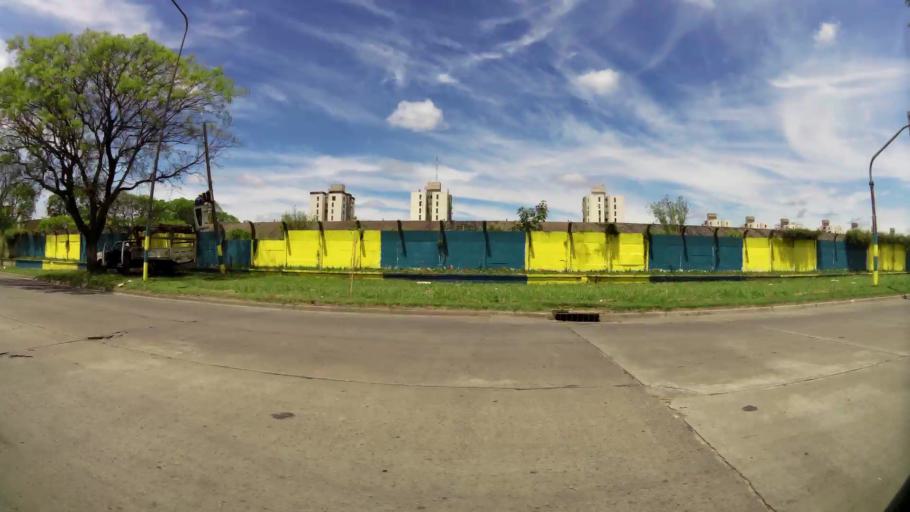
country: AR
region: Santa Fe
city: Gobernador Galvez
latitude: -32.9899
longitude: -60.6243
